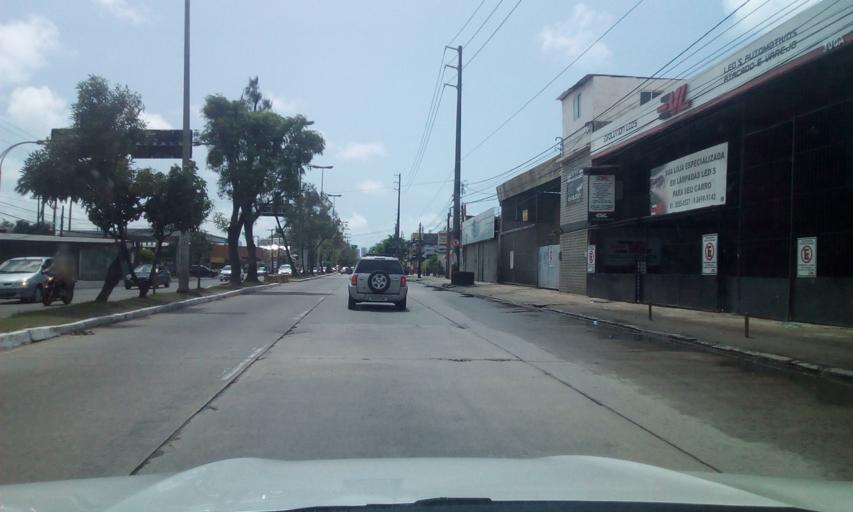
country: BR
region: Pernambuco
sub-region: Recife
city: Recife
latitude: -8.0634
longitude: -34.9339
